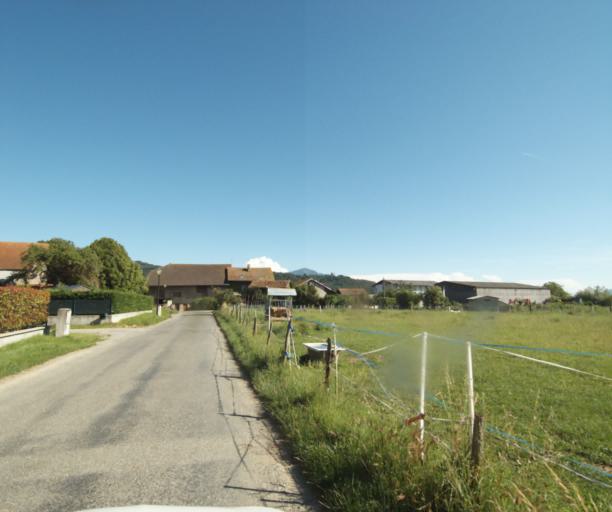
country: FR
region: Rhone-Alpes
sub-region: Departement de la Haute-Savoie
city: Massongy
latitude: 46.3225
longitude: 6.3211
